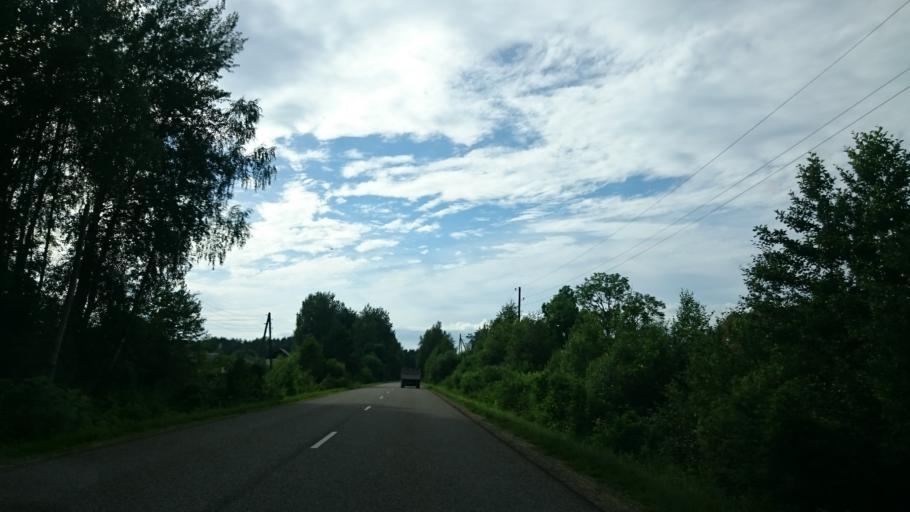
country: LV
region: Saulkrastu
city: Saulkrasti
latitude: 57.2393
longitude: 24.4456
